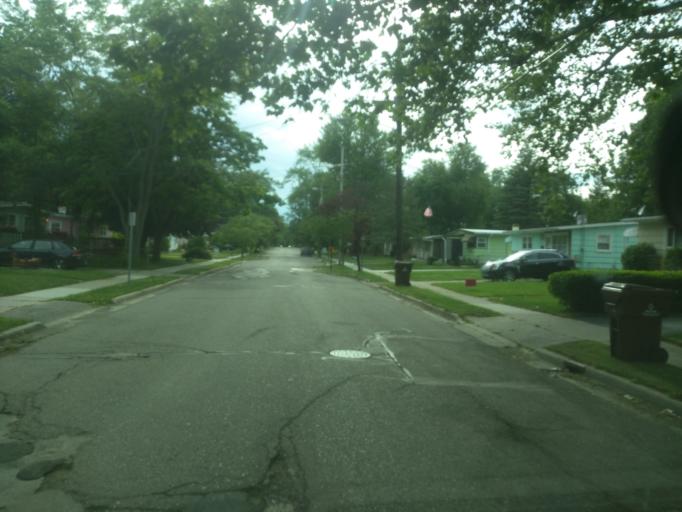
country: US
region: Michigan
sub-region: Ingham County
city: Lansing
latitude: 42.6912
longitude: -84.5779
